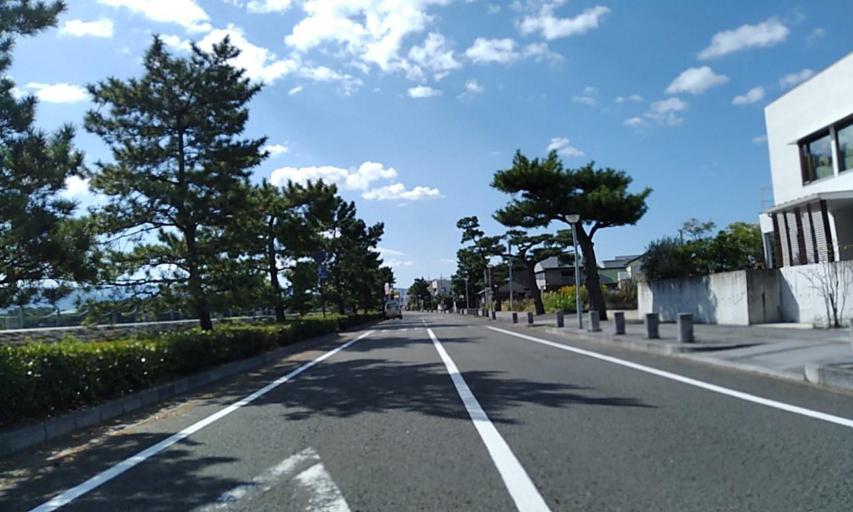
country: JP
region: Wakayama
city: Minato
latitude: 34.1858
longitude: 135.1724
